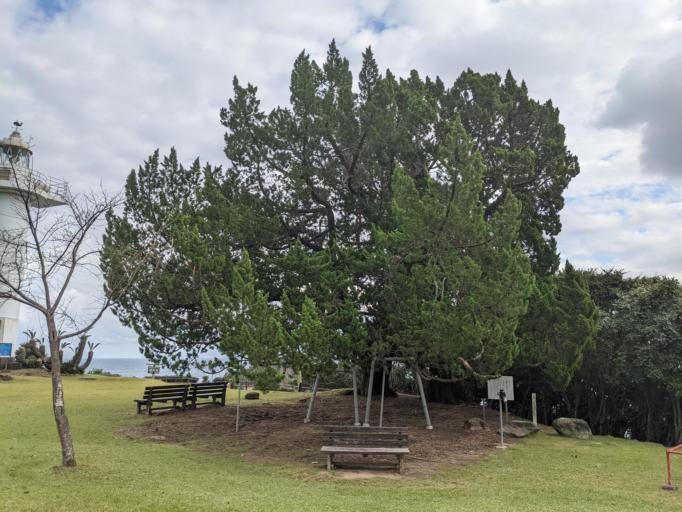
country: JP
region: Wakayama
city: Shingu
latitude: 33.5824
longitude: 135.9580
